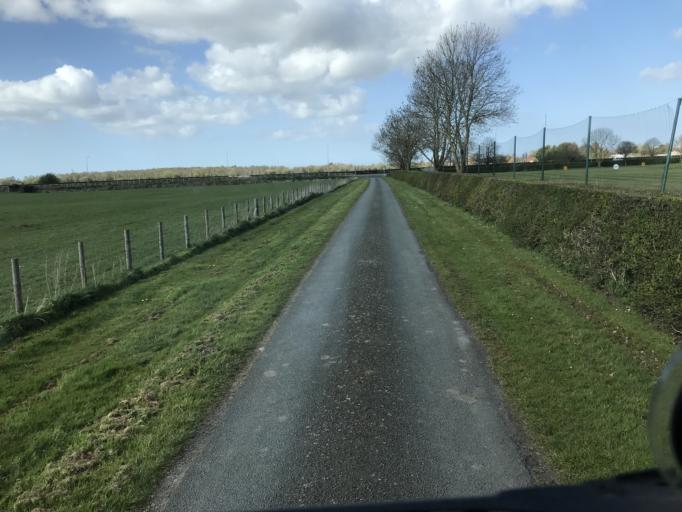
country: GB
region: England
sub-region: Cheshire West and Chester
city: Blacon
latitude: 53.1733
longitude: -2.9478
